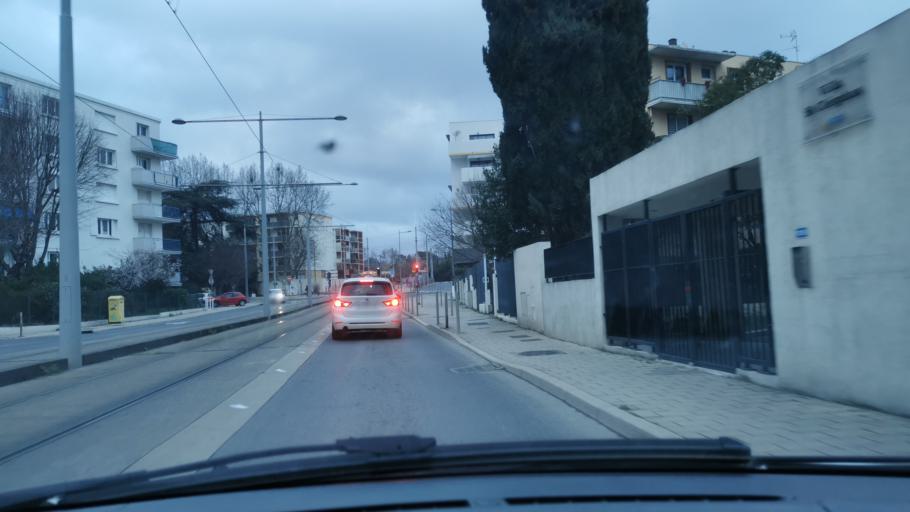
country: FR
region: Languedoc-Roussillon
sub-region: Departement de l'Herault
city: Montpellier
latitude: 43.5938
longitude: 3.8754
